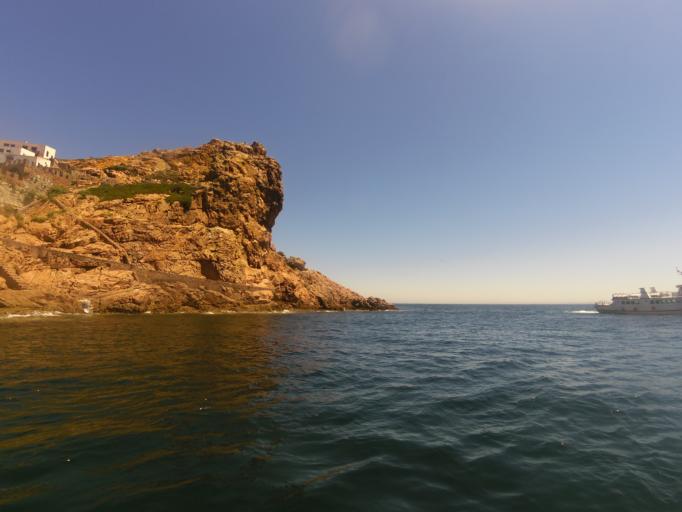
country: PT
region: Leiria
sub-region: Peniche
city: Peniche
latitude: 39.4136
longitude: -9.5062
